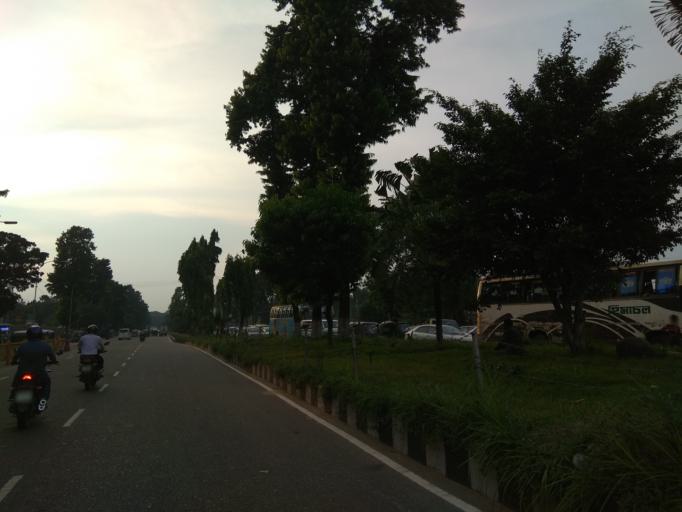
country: BD
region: Dhaka
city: Azimpur
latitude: 23.7644
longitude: 90.3886
